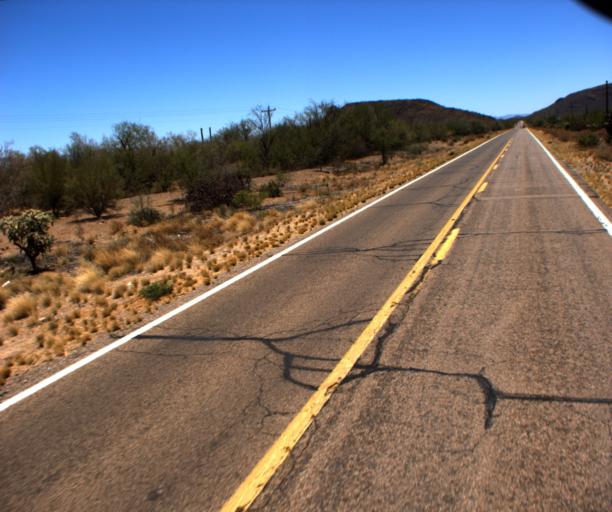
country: US
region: Arizona
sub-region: Pima County
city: Sells
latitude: 31.9780
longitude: -111.9667
